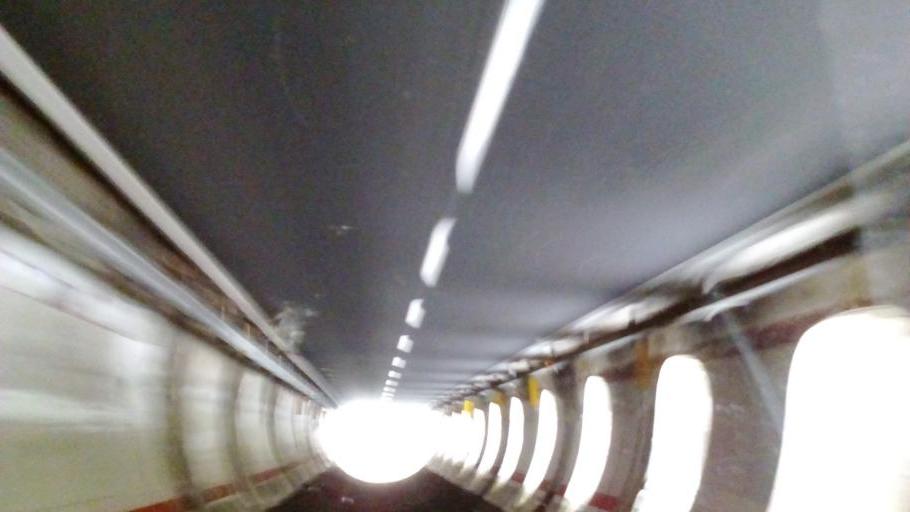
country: IT
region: Sicily
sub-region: Enna
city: Calascibetta
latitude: 37.5792
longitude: 14.2751
